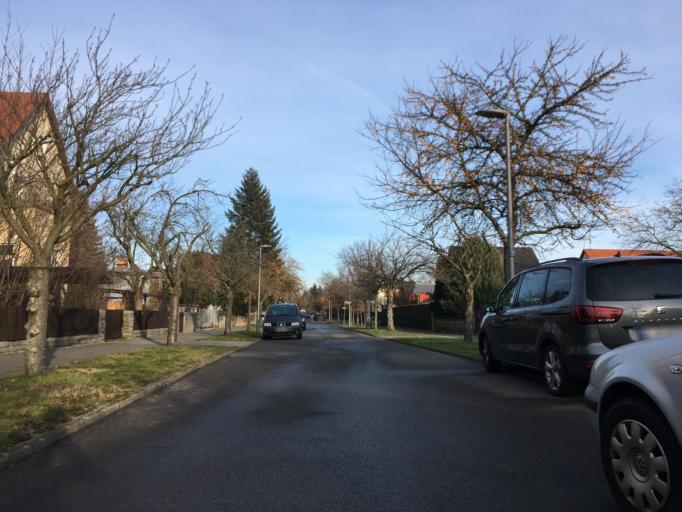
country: DE
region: Berlin
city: Blankenburg
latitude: 52.6106
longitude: 13.4602
